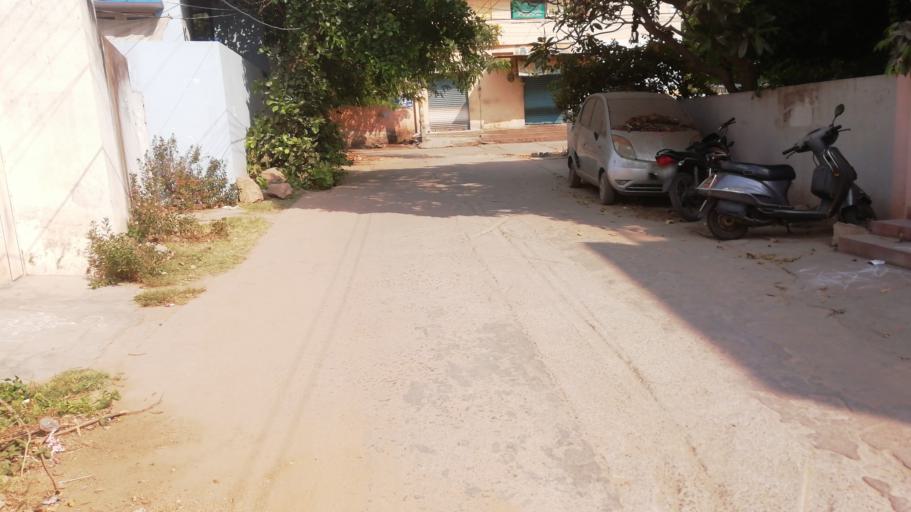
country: IN
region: Telangana
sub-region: Rangareddi
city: Gaddi Annaram
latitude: 17.3629
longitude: 78.5327
